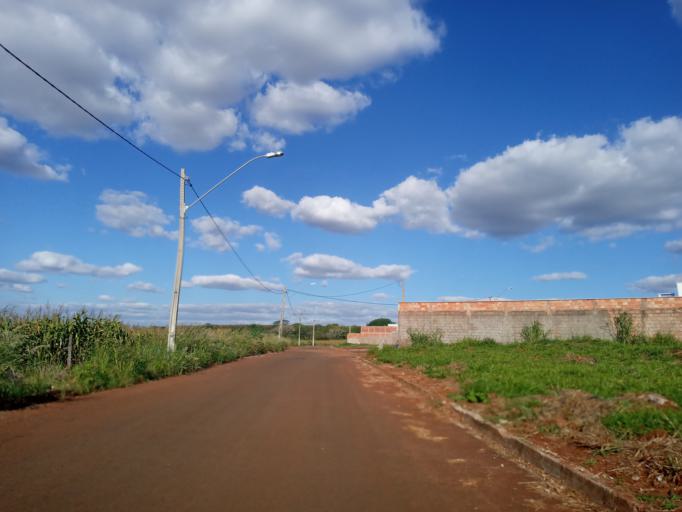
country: BR
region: Minas Gerais
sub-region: Ituiutaba
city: Ituiutaba
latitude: -18.9616
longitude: -49.4388
